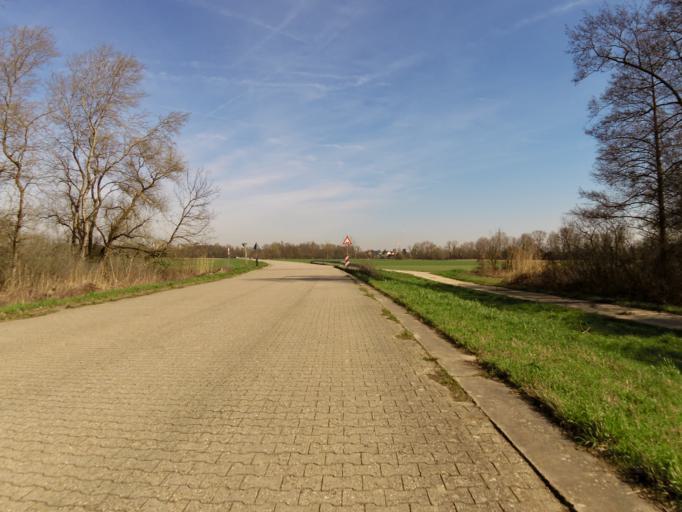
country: DE
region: Hesse
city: Gernsheim
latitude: 49.7420
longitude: 8.4714
